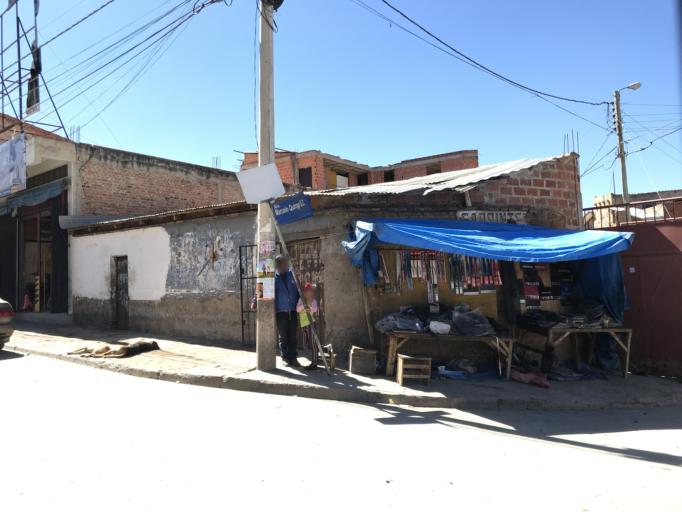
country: BO
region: Chuquisaca
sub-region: Provincia Oropeza
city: Huata
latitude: -19.0316
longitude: -65.2451
